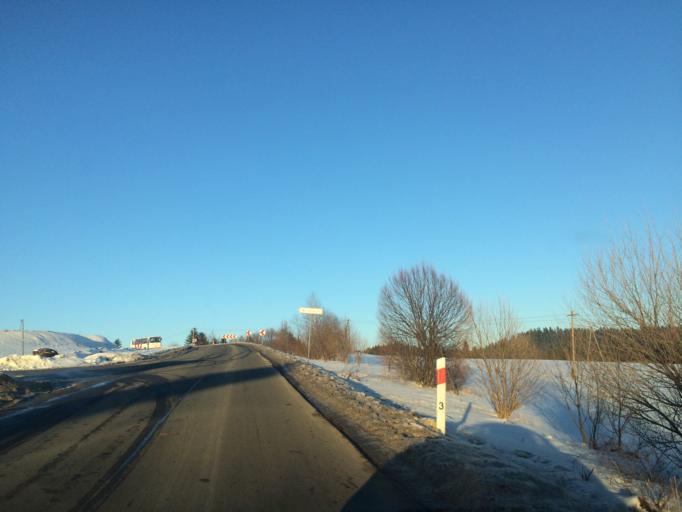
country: PL
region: Subcarpathian Voivodeship
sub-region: Powiat bieszczadzki
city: Lutowiska
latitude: 49.2636
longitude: 22.6846
